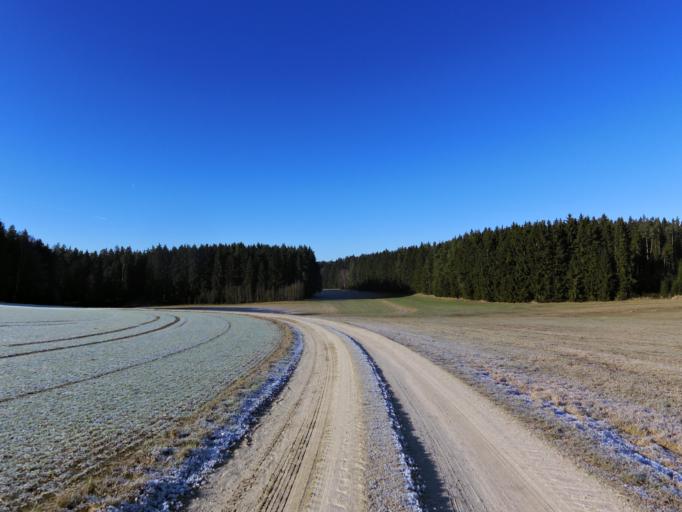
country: DE
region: Bavaria
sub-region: Upper Franconia
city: Wunsiedel
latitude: 50.0676
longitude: 12.0207
